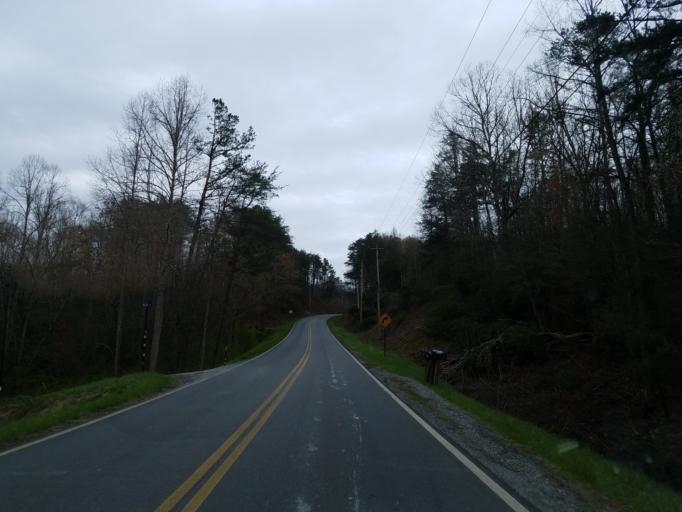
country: US
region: Georgia
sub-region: Fannin County
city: Blue Ridge
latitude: 34.8569
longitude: -84.3016
